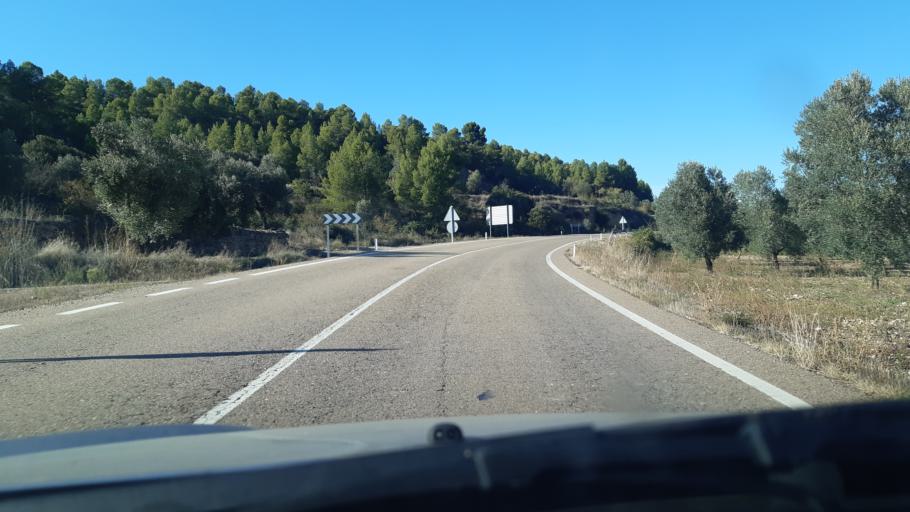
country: ES
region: Aragon
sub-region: Provincia de Teruel
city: Torre del Compte
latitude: 40.8909
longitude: 0.1074
